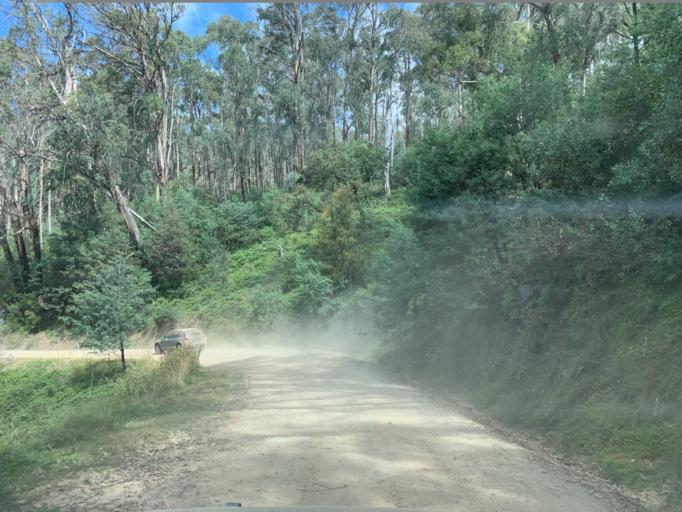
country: AU
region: Victoria
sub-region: Mansfield
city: Mansfield
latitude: -37.1002
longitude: 146.4991
